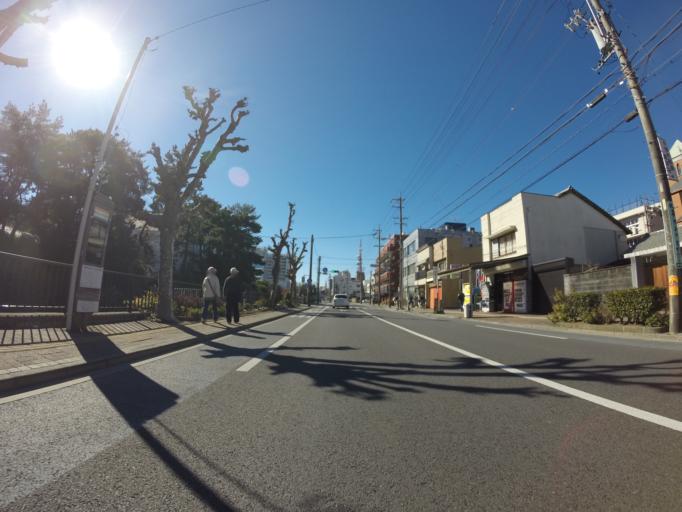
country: JP
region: Shizuoka
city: Shizuoka-shi
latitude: 34.9818
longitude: 138.3804
